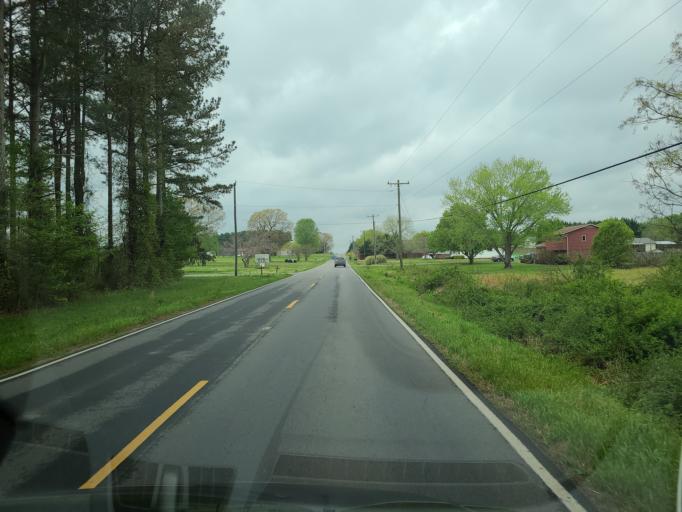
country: US
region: North Carolina
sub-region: Lincoln County
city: Lincolnton
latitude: 35.4570
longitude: -81.3037
